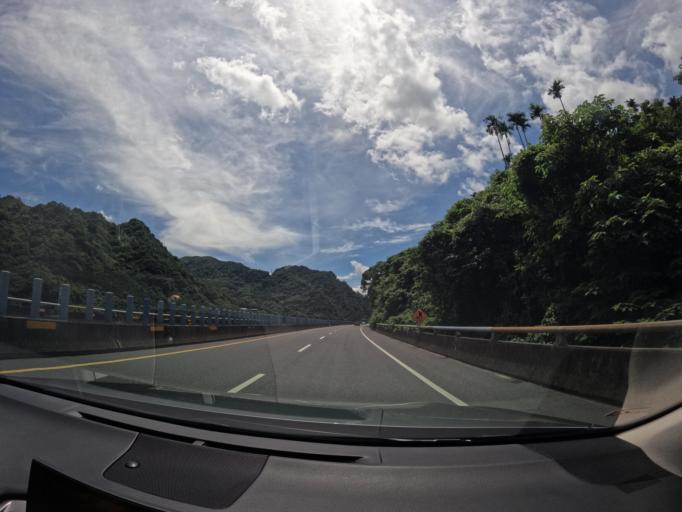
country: TW
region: Taiwan
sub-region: Miaoli
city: Miaoli
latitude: 24.4648
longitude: 120.8415
